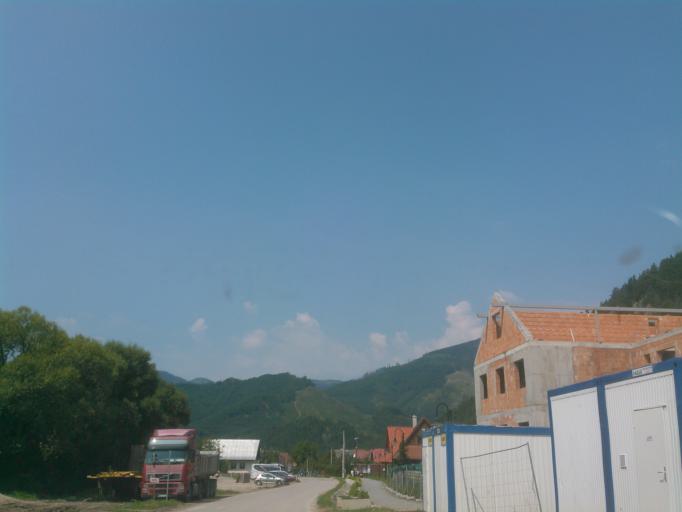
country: SK
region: Zilinsky
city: Ruzomberok
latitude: 48.9485
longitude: 19.2765
